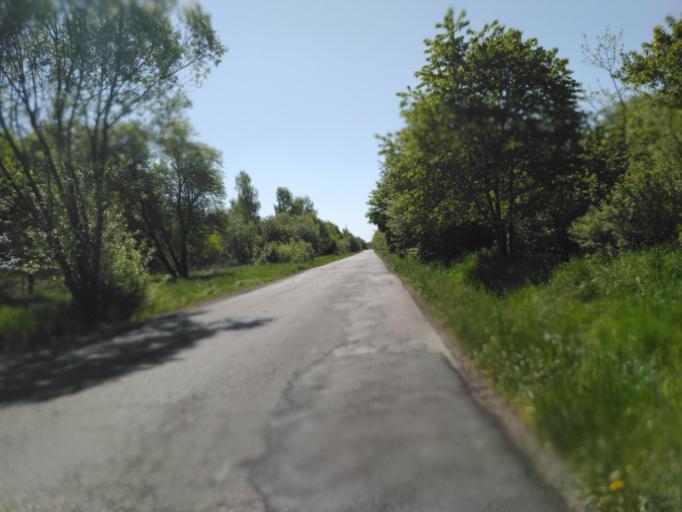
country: PL
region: Subcarpathian Voivodeship
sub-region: Krosno
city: Krosno
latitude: 49.6709
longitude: 21.7912
